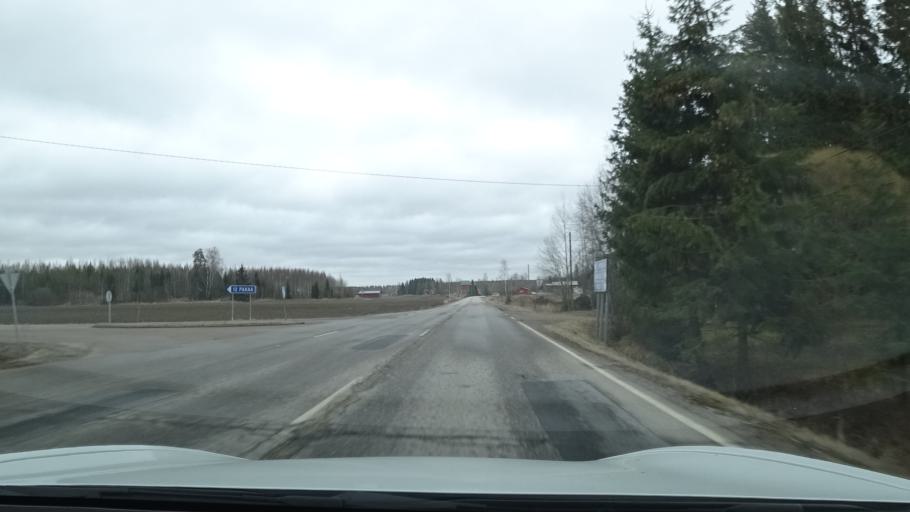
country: FI
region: Uusimaa
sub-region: Porvoo
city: Pukkila
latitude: 60.6611
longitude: 25.7002
